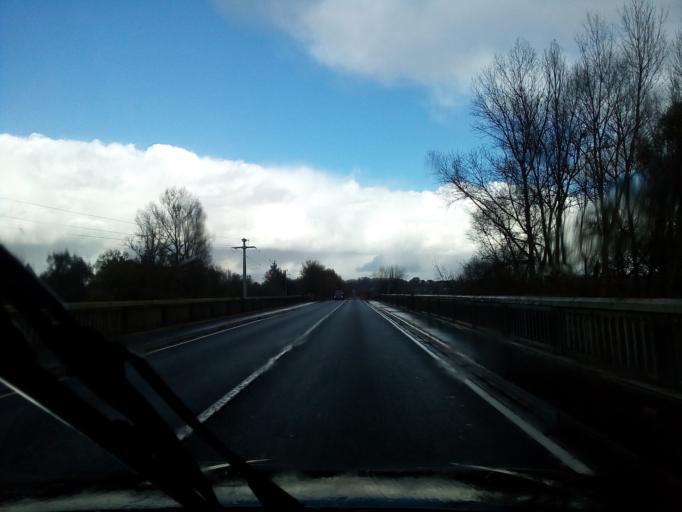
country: FR
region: Auvergne
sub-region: Departement de l'Allier
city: Varennes-sur-Allier
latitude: 46.3224
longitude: 3.3655
